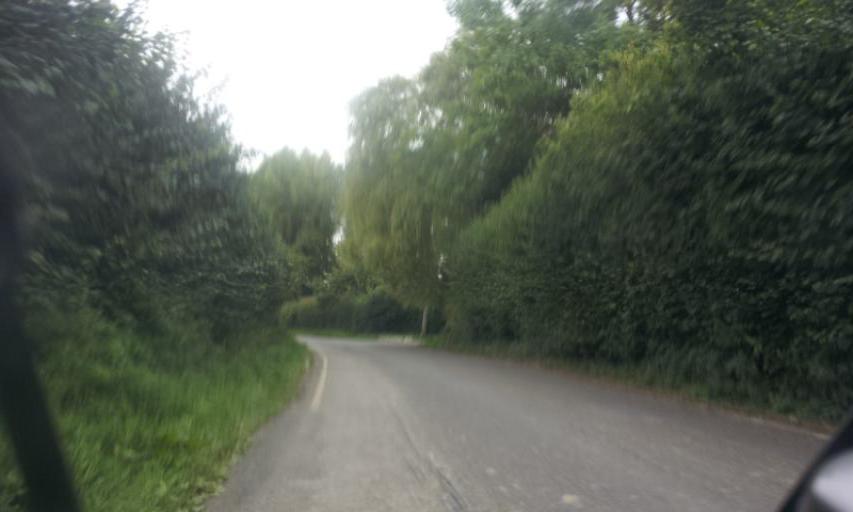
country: GB
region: England
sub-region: Kent
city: Hadlow
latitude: 51.2046
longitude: 0.3346
